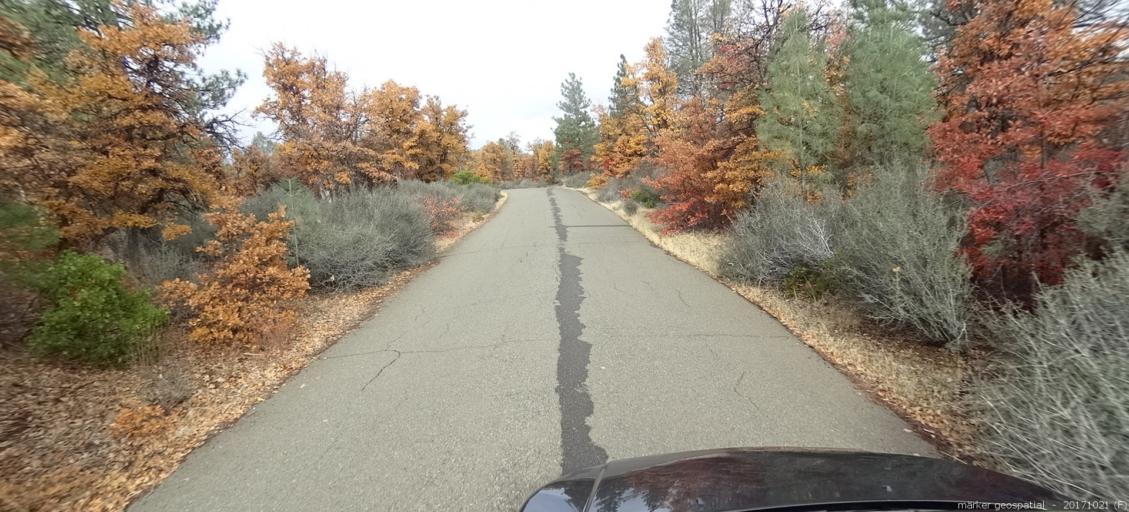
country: US
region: California
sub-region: Shasta County
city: Burney
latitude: 40.9662
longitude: -121.5705
